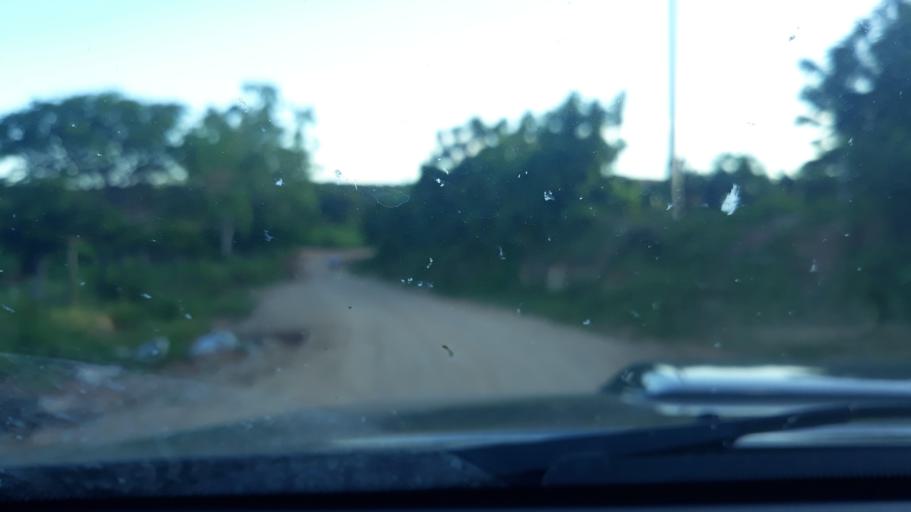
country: BR
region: Bahia
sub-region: Riacho De Santana
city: Riacho de Santana
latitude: -13.8268
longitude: -42.7275
